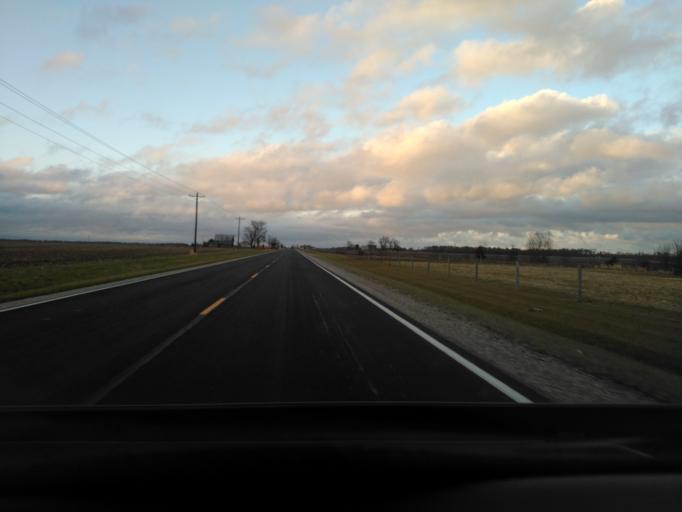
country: US
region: Illinois
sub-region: Effingham County
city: Altamont
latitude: 38.9965
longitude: -88.7486
